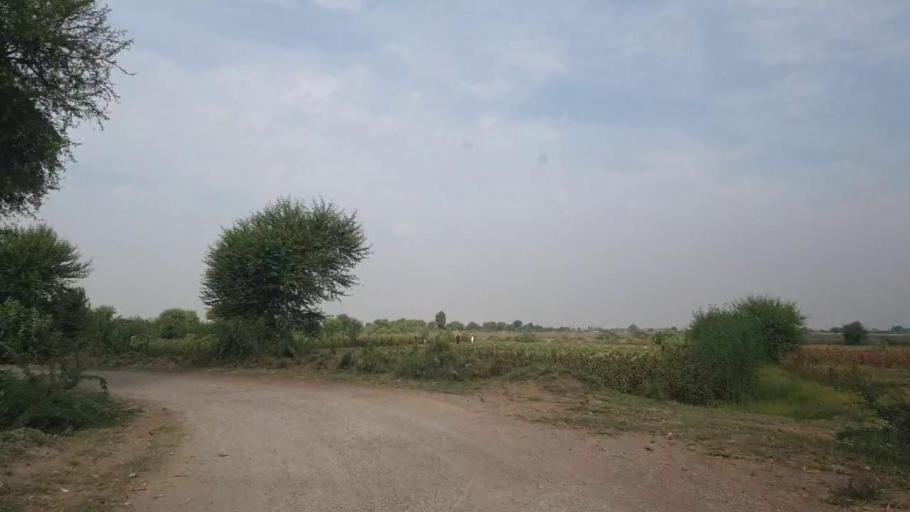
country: PK
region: Sindh
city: Rajo Khanani
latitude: 24.9724
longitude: 68.9959
